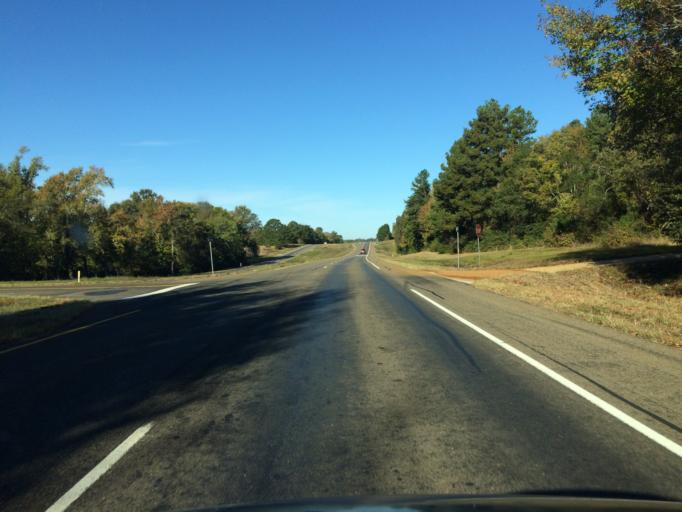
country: US
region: Texas
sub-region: Wood County
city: Hawkins
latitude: 32.5897
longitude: -95.2193
